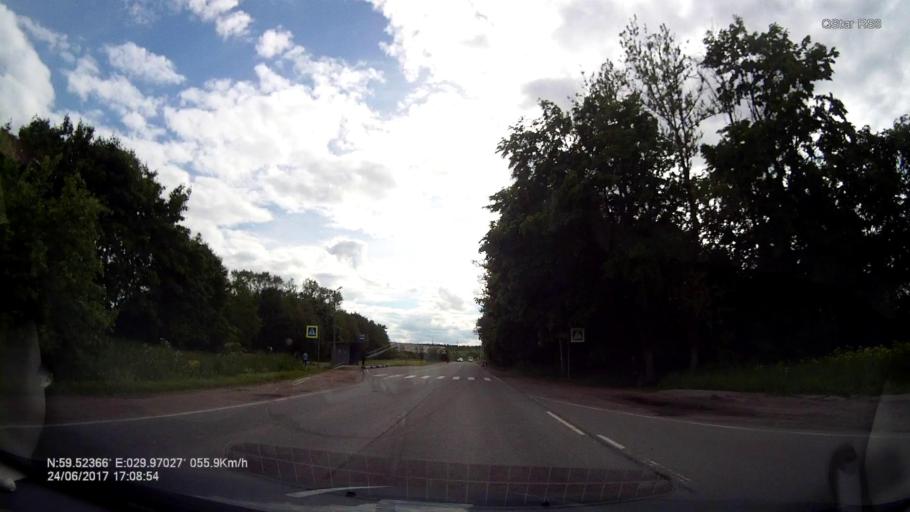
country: RU
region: Leningrad
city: Voyskovitsy
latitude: 59.5235
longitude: 29.9697
